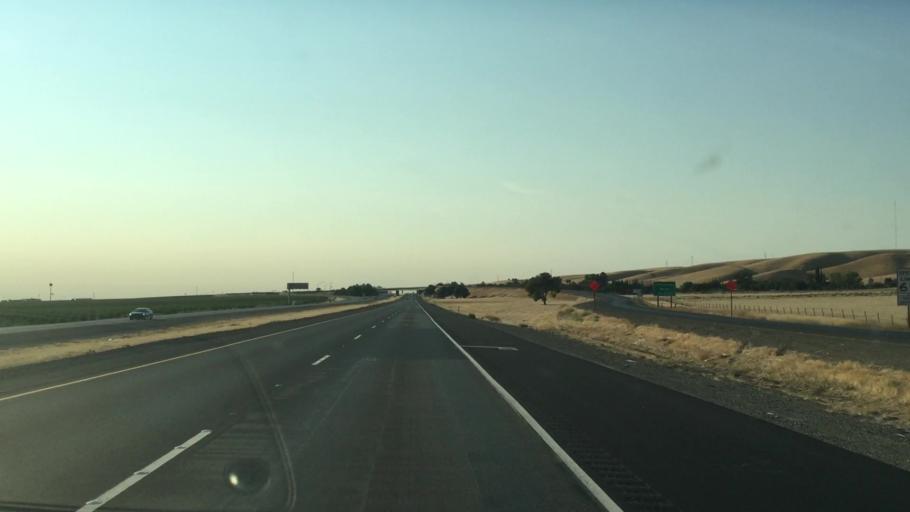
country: US
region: California
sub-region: San Joaquin County
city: Tracy
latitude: 37.6448
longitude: -121.4111
